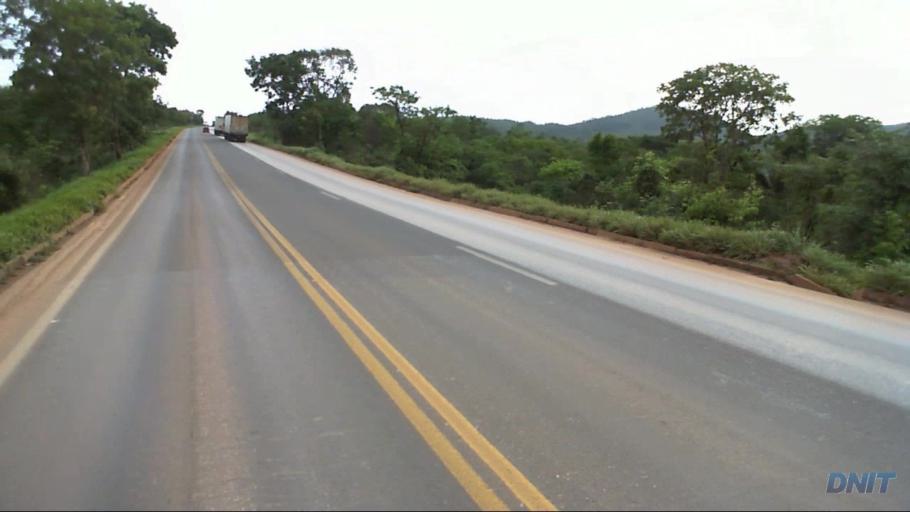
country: BR
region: Goias
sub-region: Uruacu
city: Uruacu
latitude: -14.5802
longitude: -49.1595
